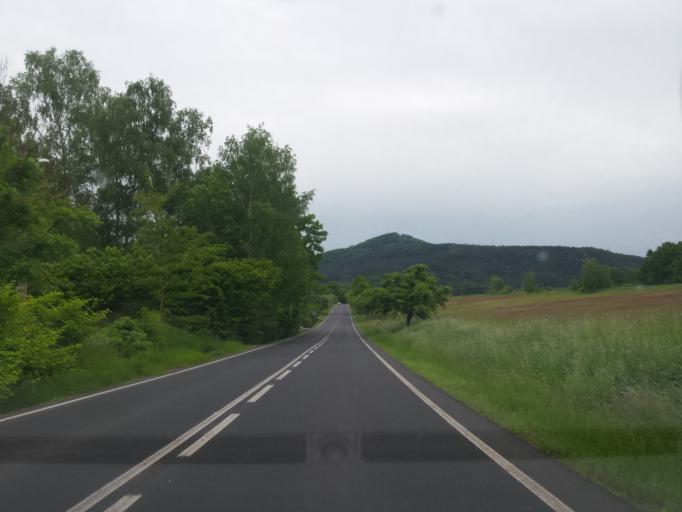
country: CZ
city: Novy Bor
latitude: 50.7465
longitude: 14.5771
